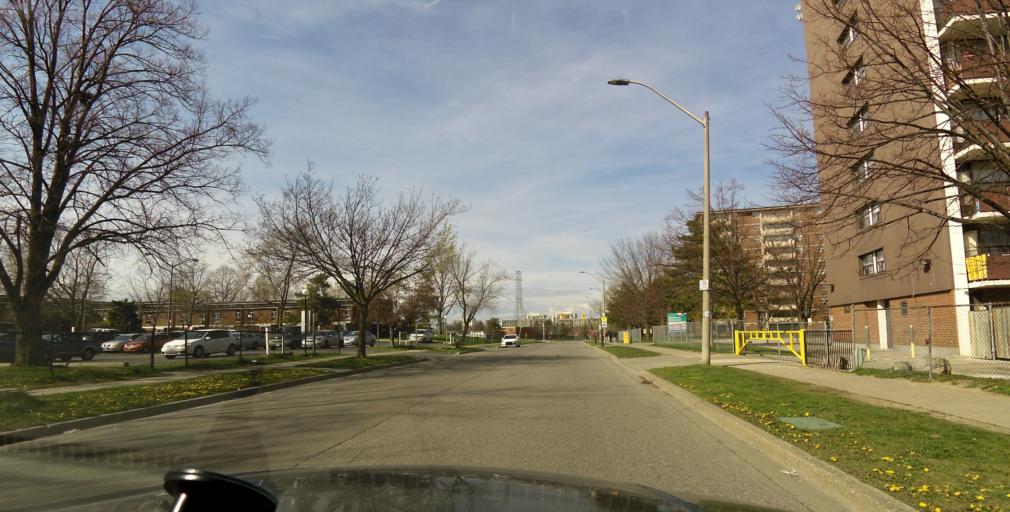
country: CA
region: Ontario
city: Etobicoke
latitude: 43.6250
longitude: -79.5897
